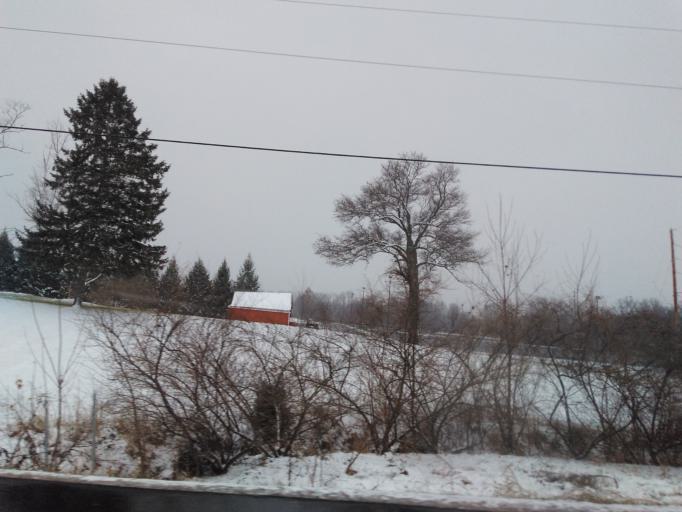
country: US
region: Illinois
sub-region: Madison County
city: Troy
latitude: 38.7176
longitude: -89.8580
